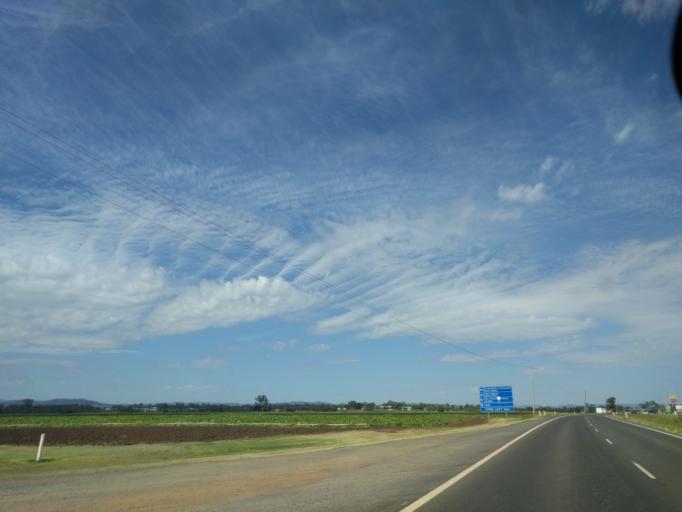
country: AU
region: Queensland
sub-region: Lockyer Valley
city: Gatton
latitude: -27.5439
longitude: 152.3518
